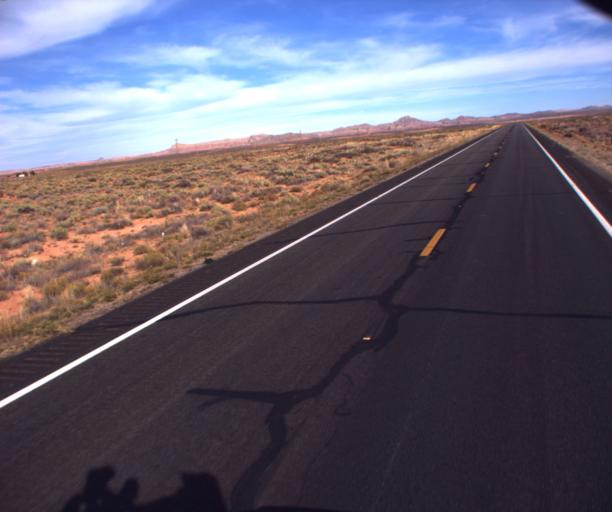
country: US
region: Arizona
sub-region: Apache County
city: Many Farms
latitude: 36.9405
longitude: -109.6685
